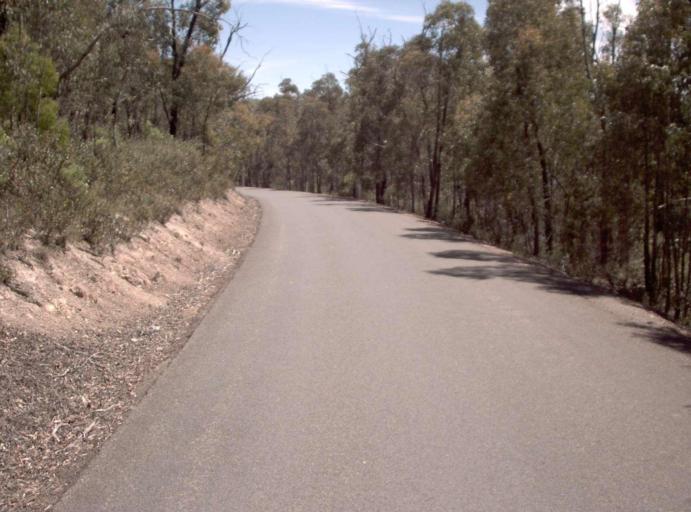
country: AU
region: New South Wales
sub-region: Snowy River
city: Jindabyne
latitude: -37.1093
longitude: 148.2516
